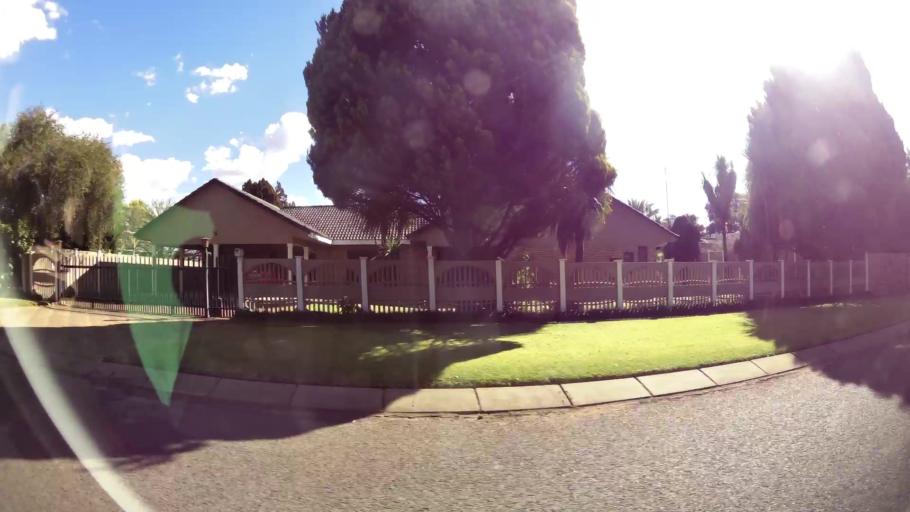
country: ZA
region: North-West
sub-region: Dr Kenneth Kaunda District Municipality
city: Klerksdorp
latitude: -26.8589
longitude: 26.6209
